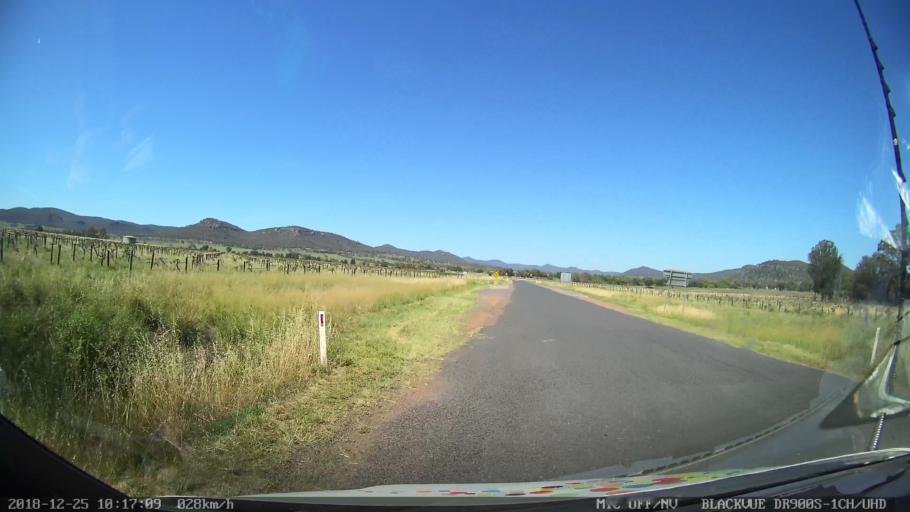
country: AU
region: New South Wales
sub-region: Muswellbrook
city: Denman
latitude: -32.3419
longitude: 150.5789
